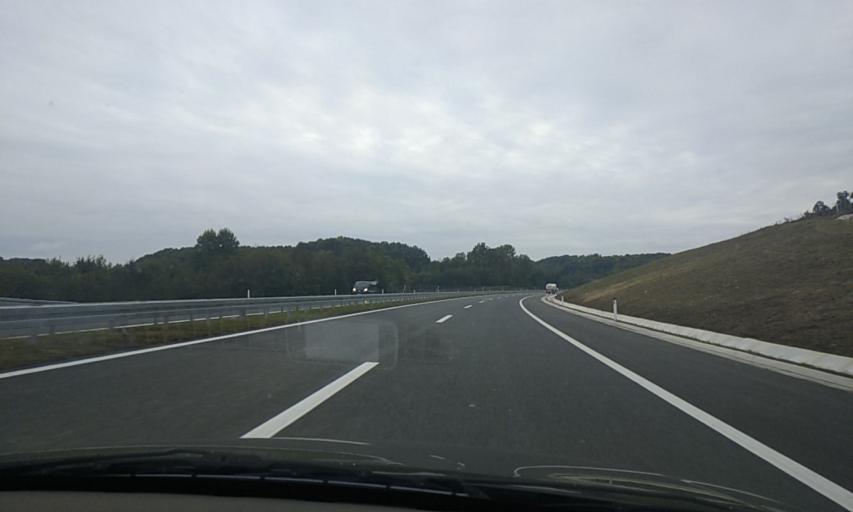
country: BA
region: Republika Srpska
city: Prnjavor
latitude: 44.8735
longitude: 17.5296
